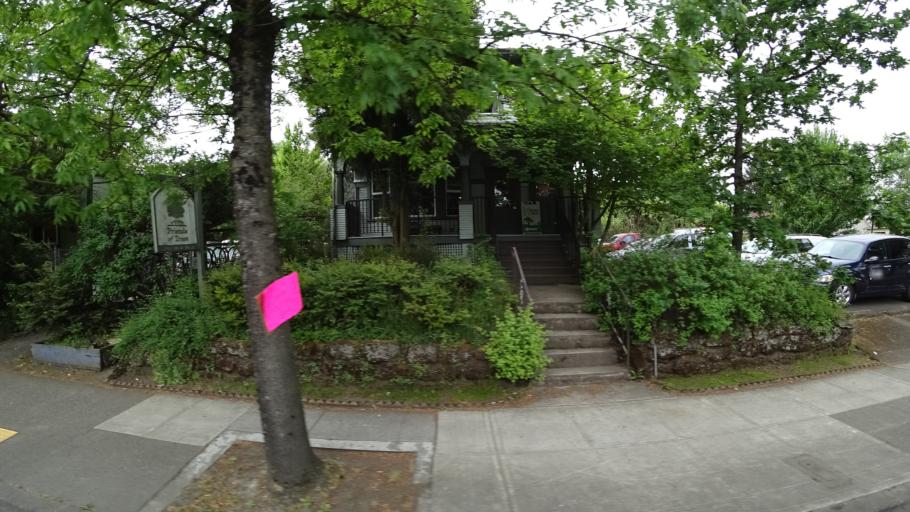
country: US
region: Oregon
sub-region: Multnomah County
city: Portland
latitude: 45.5457
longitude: -122.6617
